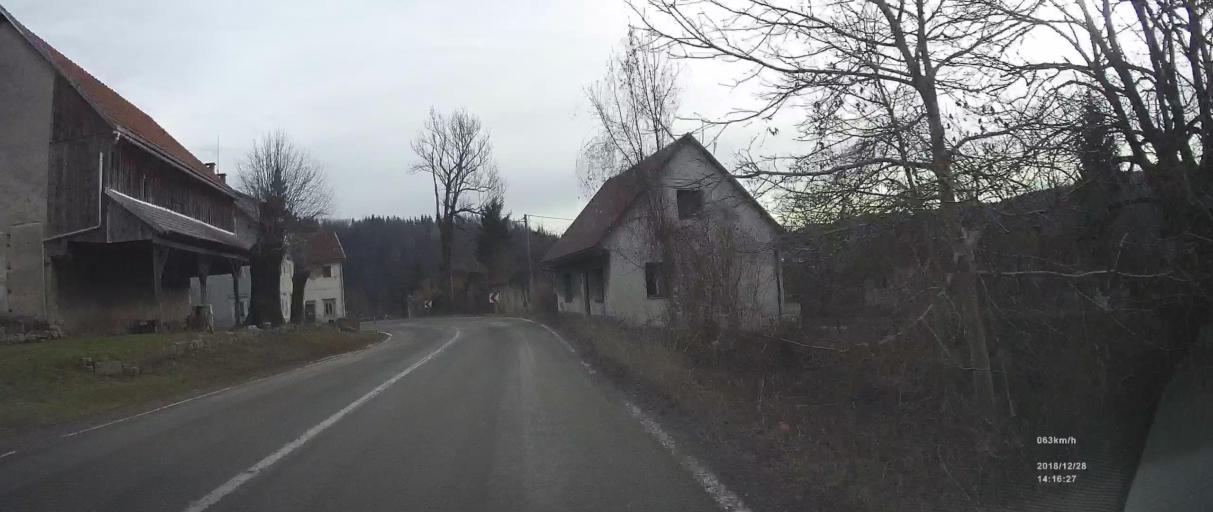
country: HR
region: Primorsko-Goranska
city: Vrbovsko
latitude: 45.4185
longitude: 15.0360
